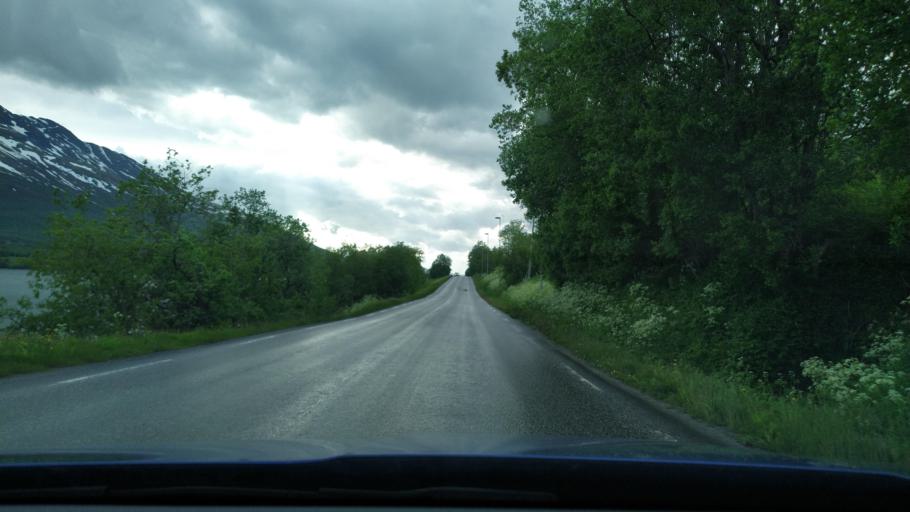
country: NO
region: Troms
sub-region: Balsfjord
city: Storsteinnes
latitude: 69.2207
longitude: 19.5327
